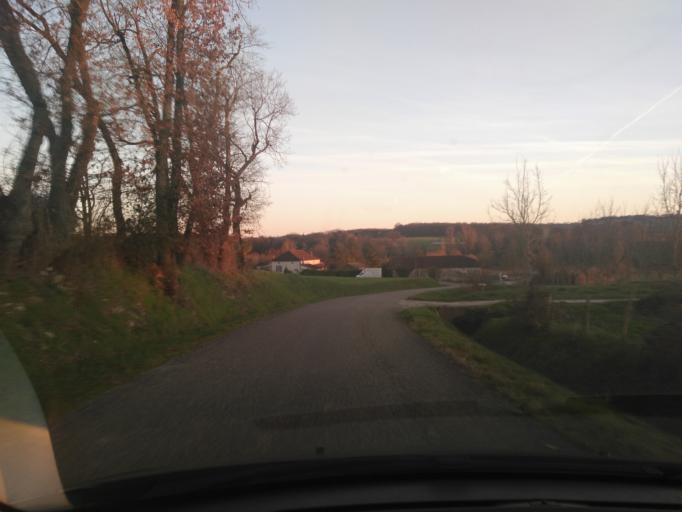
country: FR
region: Aquitaine
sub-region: Departement du Lot-et-Garonne
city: Villeneuve-sur-Lot
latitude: 44.4635
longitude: 0.7197
